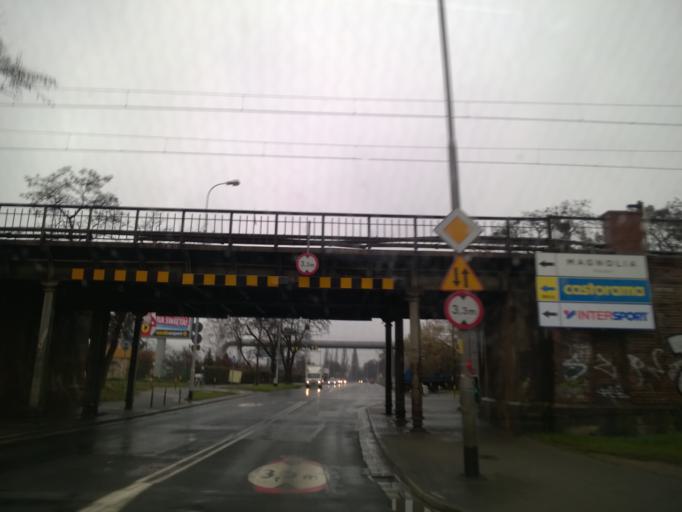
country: PL
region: Lower Silesian Voivodeship
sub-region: Powiat wroclawski
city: Wroclaw
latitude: 51.1222
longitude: 17.0121
